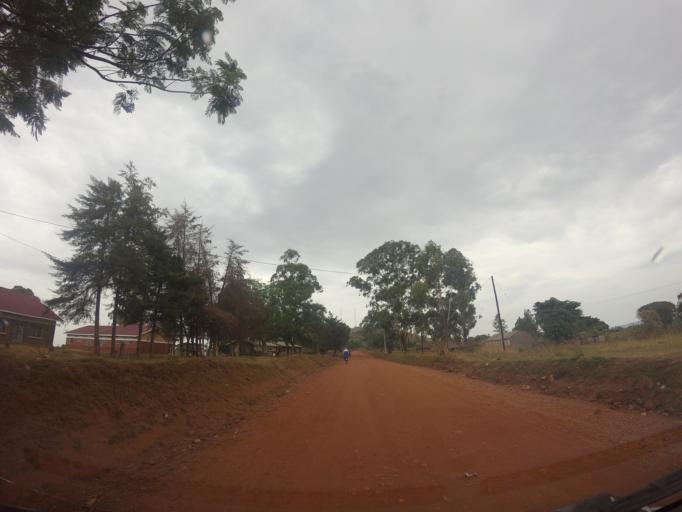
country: UG
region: Northern Region
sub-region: Zombo District
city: Zombo
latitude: 2.7607
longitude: 30.8531
